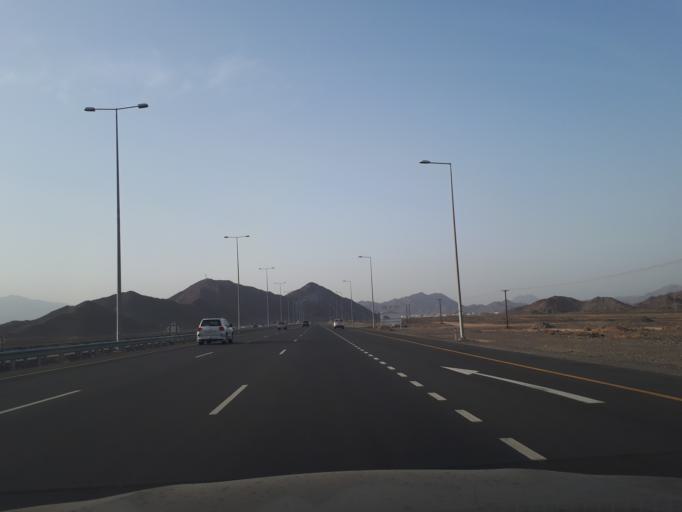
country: OM
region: Muhafazat ad Dakhiliyah
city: Sufalat Sama'il
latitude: 23.2990
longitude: 58.1107
